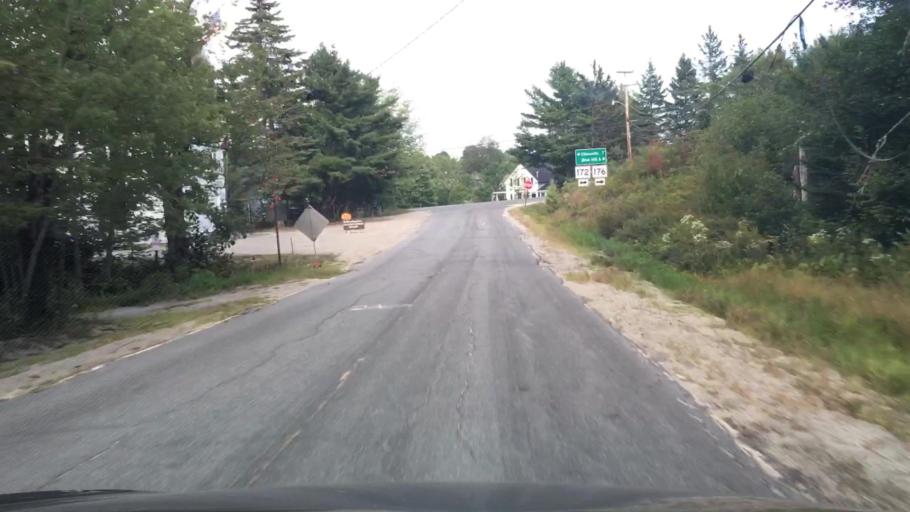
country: US
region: Maine
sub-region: Hancock County
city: Surry
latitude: 44.4942
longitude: -68.5080
